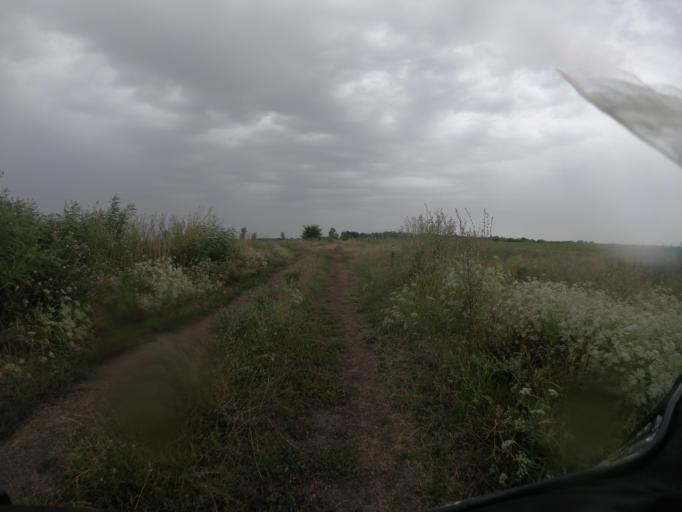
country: HU
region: Heves
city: Poroszlo
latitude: 47.6969
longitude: 20.5861
